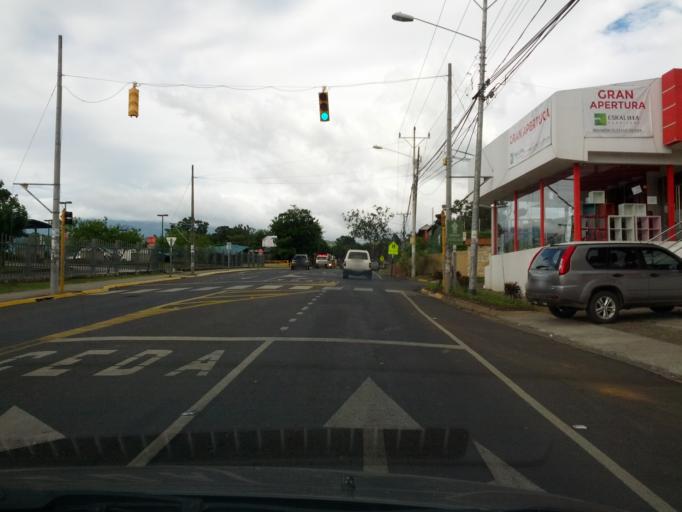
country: CR
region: Alajuela
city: Alajuela
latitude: 10.0274
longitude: -84.2155
